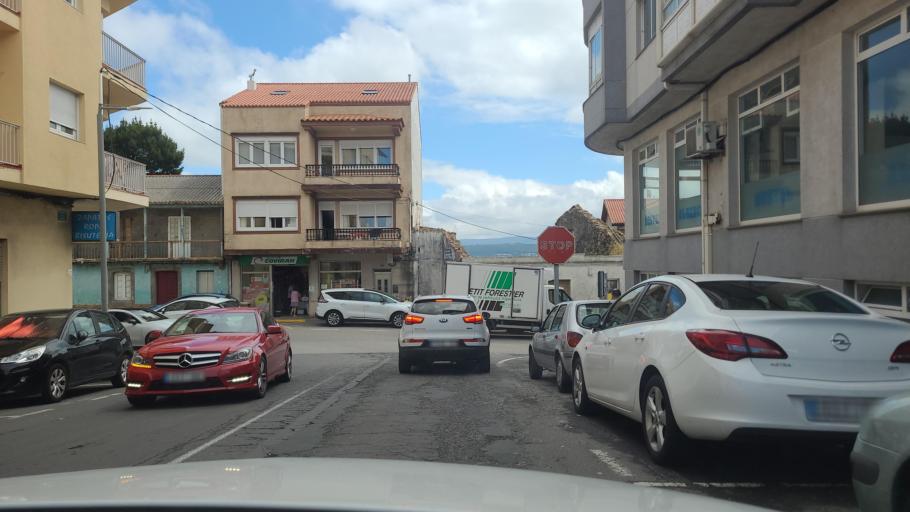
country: ES
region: Galicia
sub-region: Provincia da Coruna
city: Fisterra
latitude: 42.9102
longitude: -9.2633
